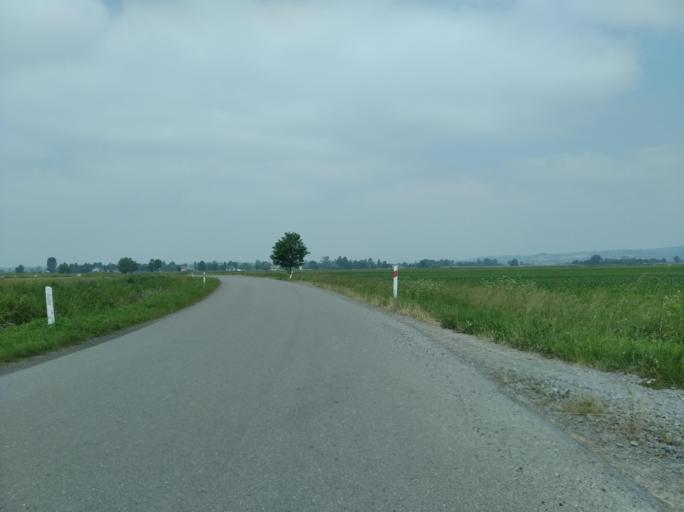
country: PL
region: Subcarpathian Voivodeship
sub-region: Powiat sanocki
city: Besko
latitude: 49.6112
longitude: 21.9553
